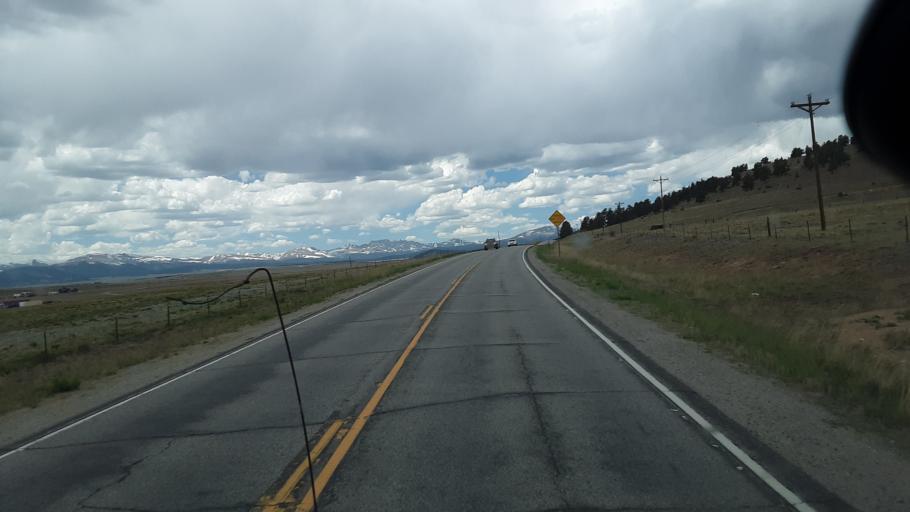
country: US
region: Colorado
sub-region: Park County
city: Fairplay
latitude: 39.0565
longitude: -105.8515
